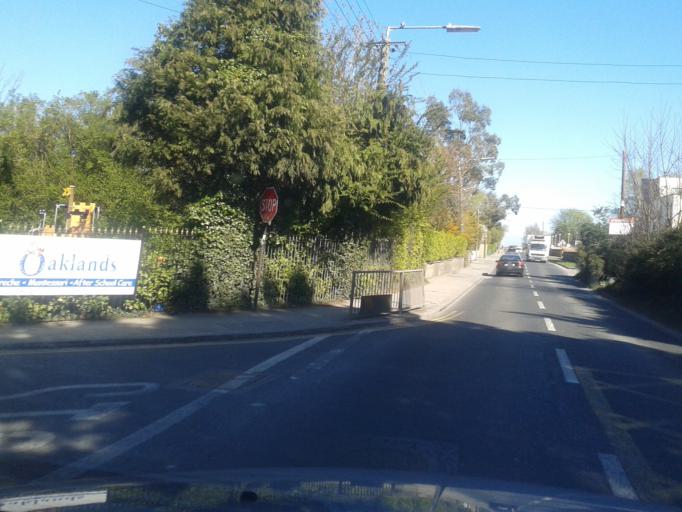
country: IE
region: Leinster
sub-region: Fingal County
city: Swords
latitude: 53.4540
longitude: -6.2099
